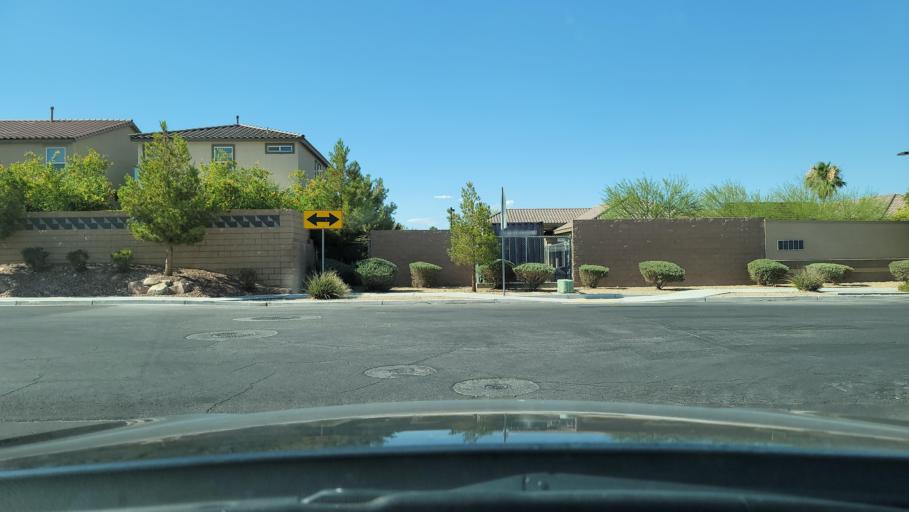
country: US
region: Nevada
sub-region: Clark County
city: Spring Valley
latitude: 36.0904
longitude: -115.2485
